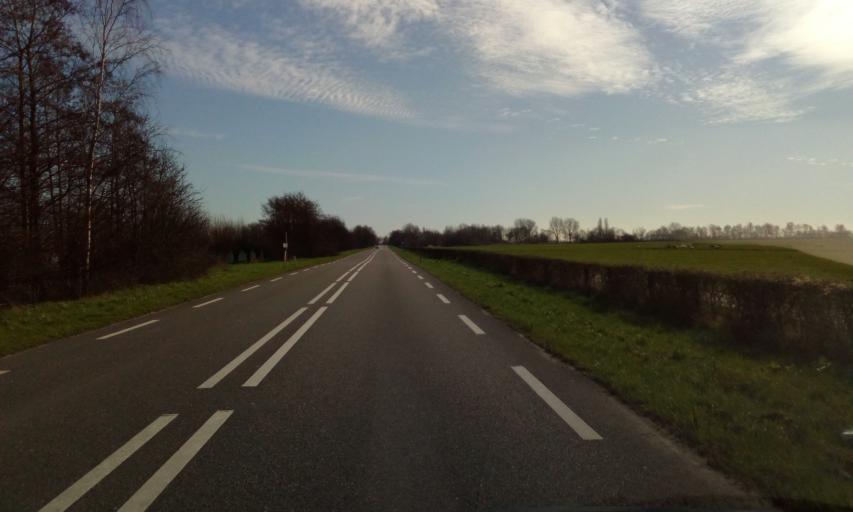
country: NL
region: South Holland
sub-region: Gemeente Alphen aan den Rijn
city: Alphen aan den Rijn
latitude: 52.1348
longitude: 4.6968
